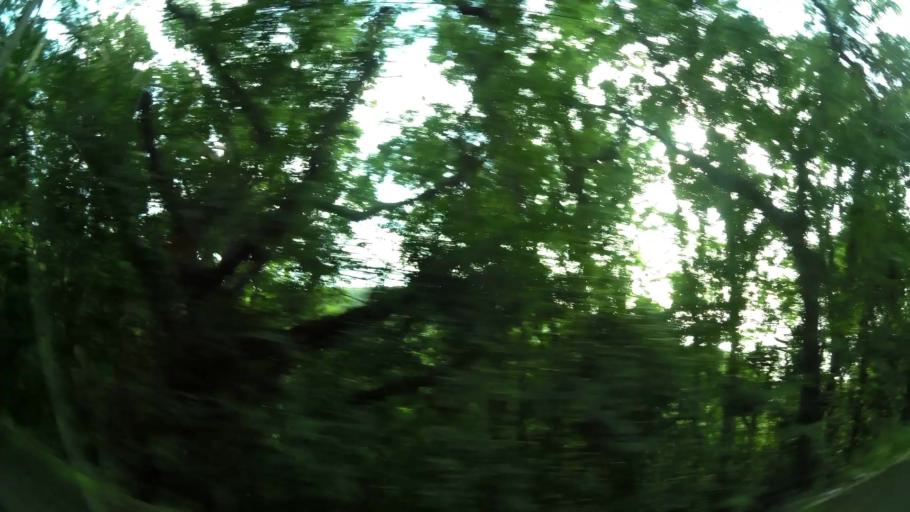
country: GP
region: Guadeloupe
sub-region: Guadeloupe
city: Pointe-Noire
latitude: 16.1887
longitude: -61.7776
